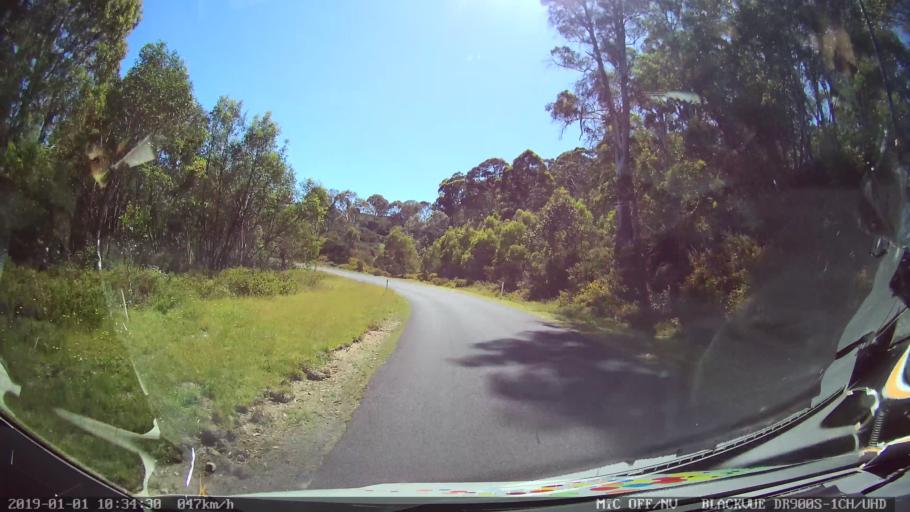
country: AU
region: New South Wales
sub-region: Snowy River
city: Jindabyne
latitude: -36.0496
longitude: 148.2837
